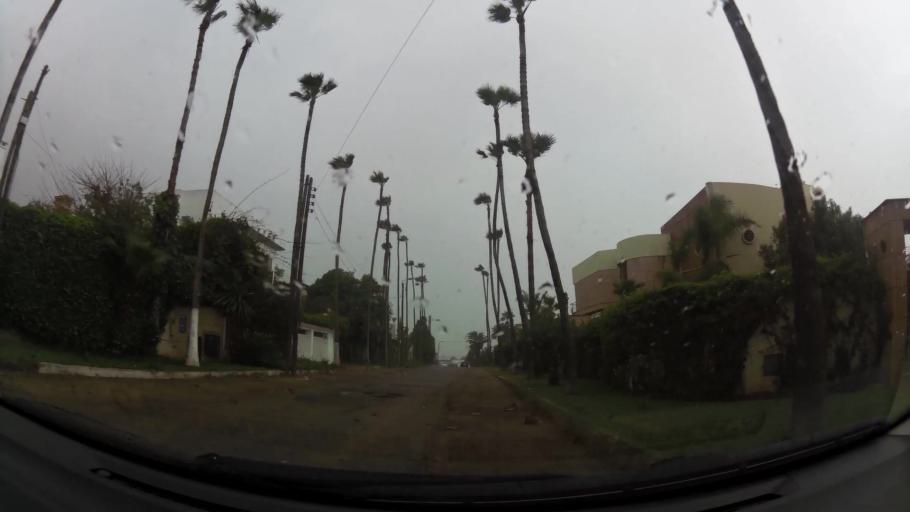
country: MA
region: Grand Casablanca
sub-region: Casablanca
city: Casablanca
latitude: 33.5885
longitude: -7.6789
